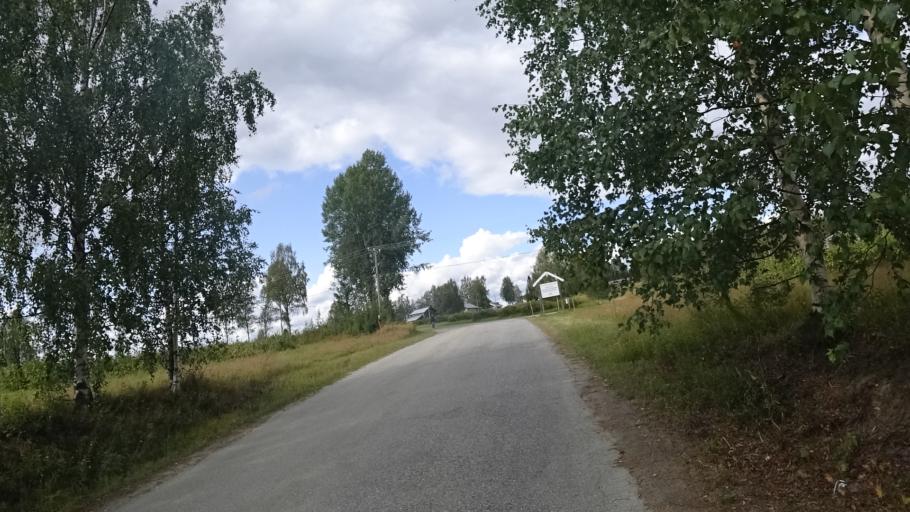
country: FI
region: North Karelia
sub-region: Joensuu
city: Ilomantsi
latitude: 62.6549
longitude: 30.9412
